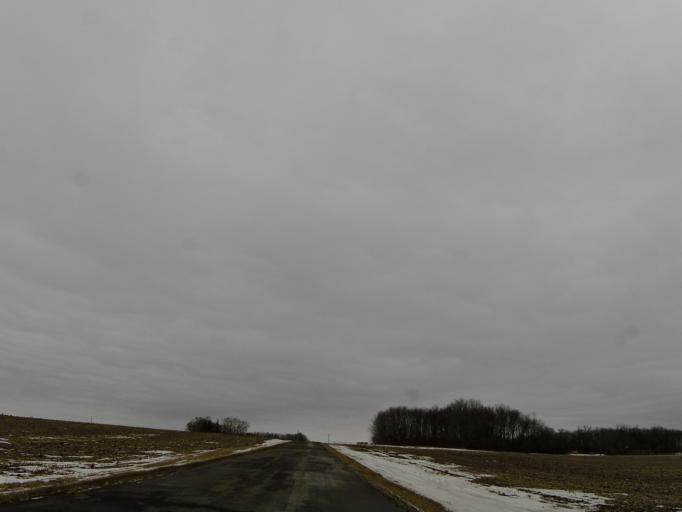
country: US
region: Minnesota
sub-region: Dakota County
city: Hastings
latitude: 44.8044
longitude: -92.8800
